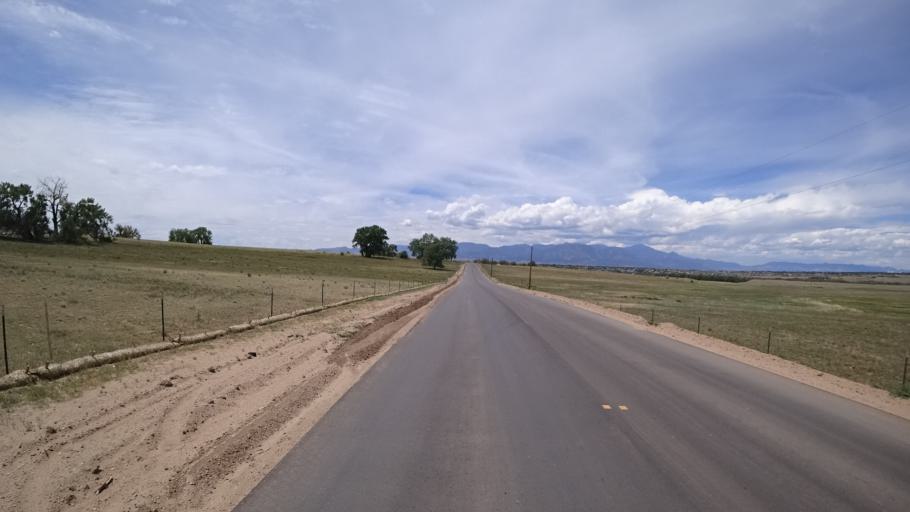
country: US
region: Colorado
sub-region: El Paso County
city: Fountain
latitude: 38.6940
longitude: -104.6582
